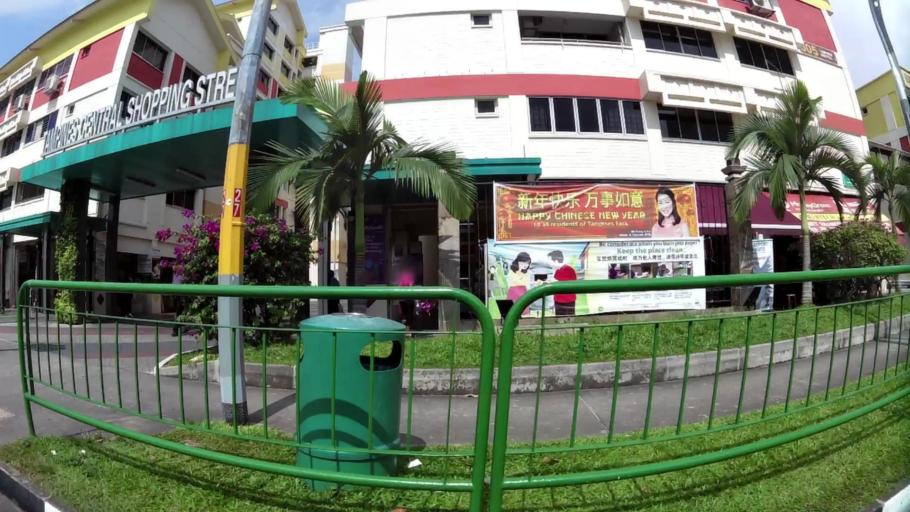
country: SG
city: Singapore
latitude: 1.3552
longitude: 103.9448
